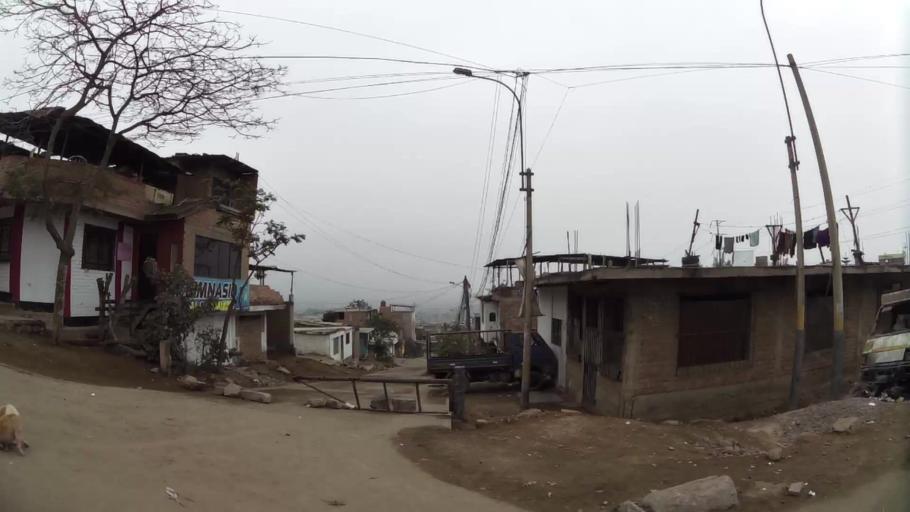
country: PE
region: Lima
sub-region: Lima
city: Surco
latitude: -12.2262
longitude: -76.9160
